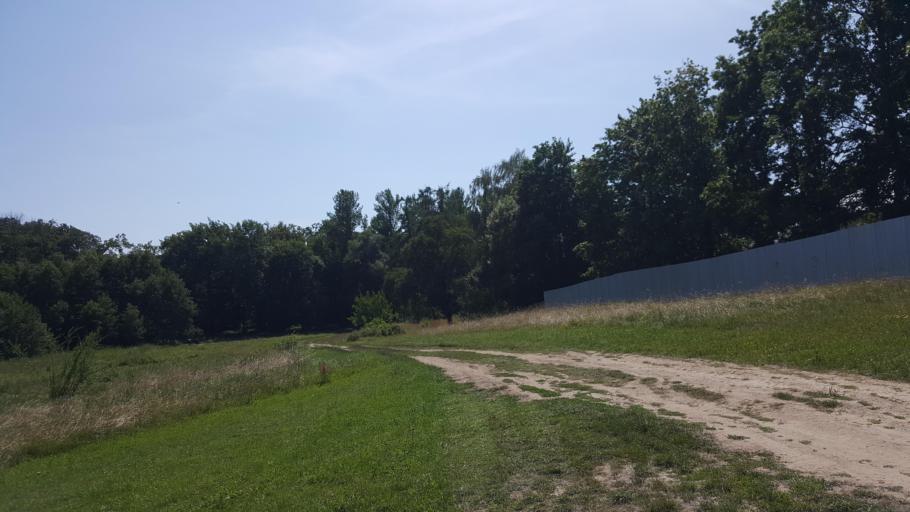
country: BY
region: Brest
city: Vysokaye
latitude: 52.3692
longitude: 23.3686
